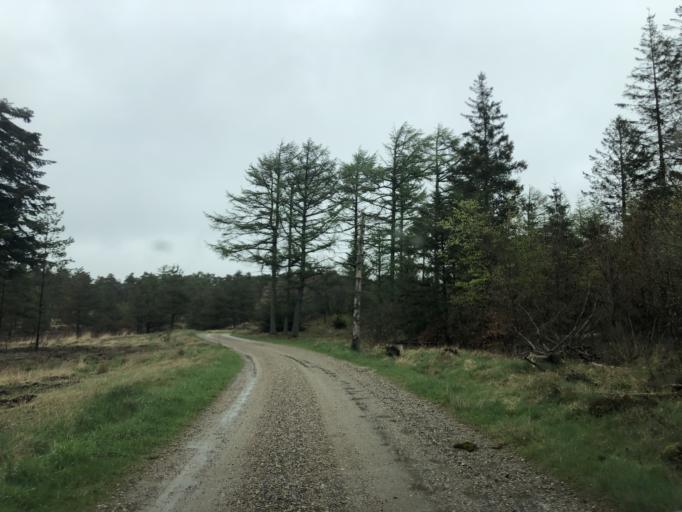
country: DK
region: Central Jutland
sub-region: Lemvig Kommune
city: Lemvig
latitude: 56.4509
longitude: 8.3926
